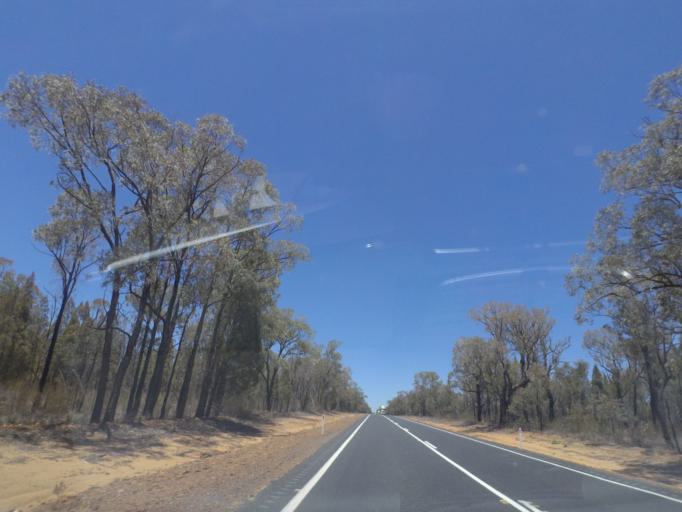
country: AU
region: New South Wales
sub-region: Narrabri
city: Narrabri
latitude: -30.7348
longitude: 149.5186
